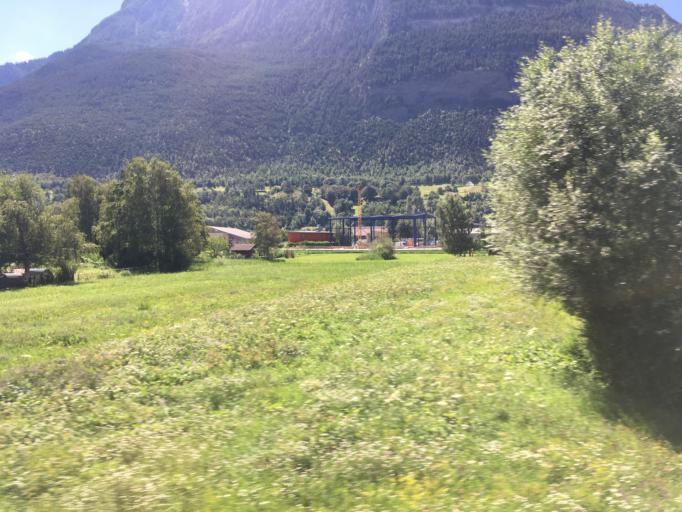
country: CH
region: Valais
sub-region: Brig District
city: Brig
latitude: 46.3091
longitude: 7.9543
